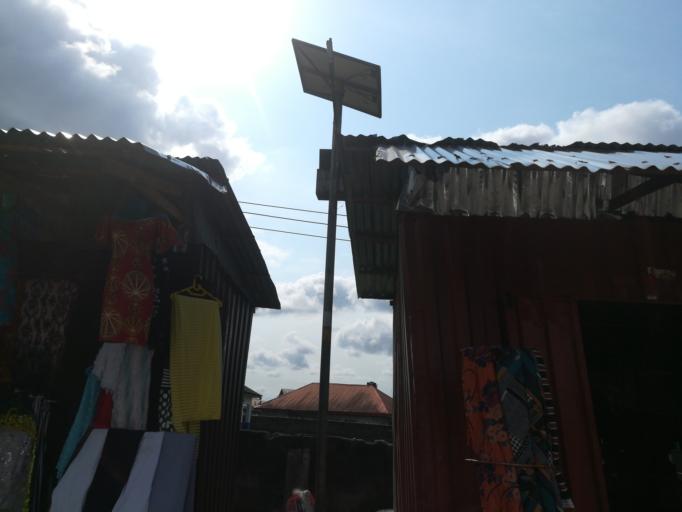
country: NG
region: Rivers
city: Okrika
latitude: 4.7642
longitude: 7.0853
